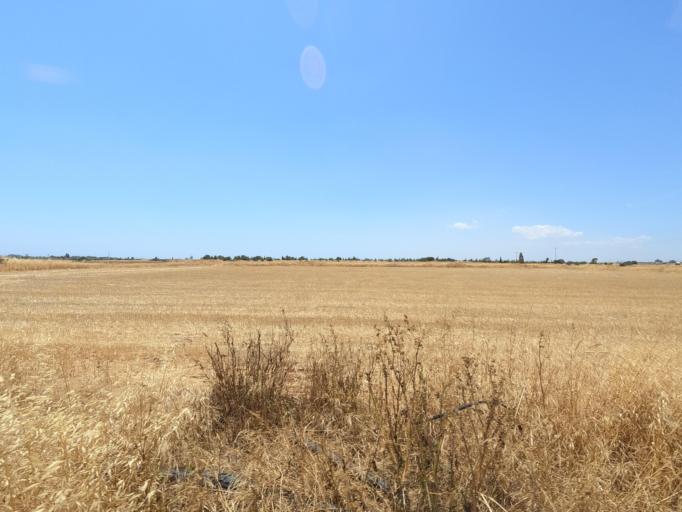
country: CY
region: Larnaka
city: Pergamos
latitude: 35.0211
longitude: 33.7168
